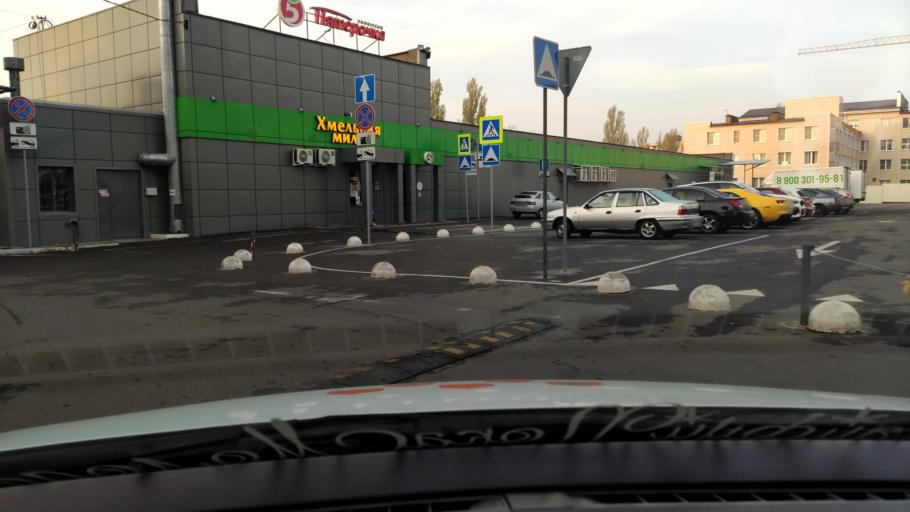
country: RU
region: Voronezj
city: Podgornoye
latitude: 51.6938
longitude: 39.1394
